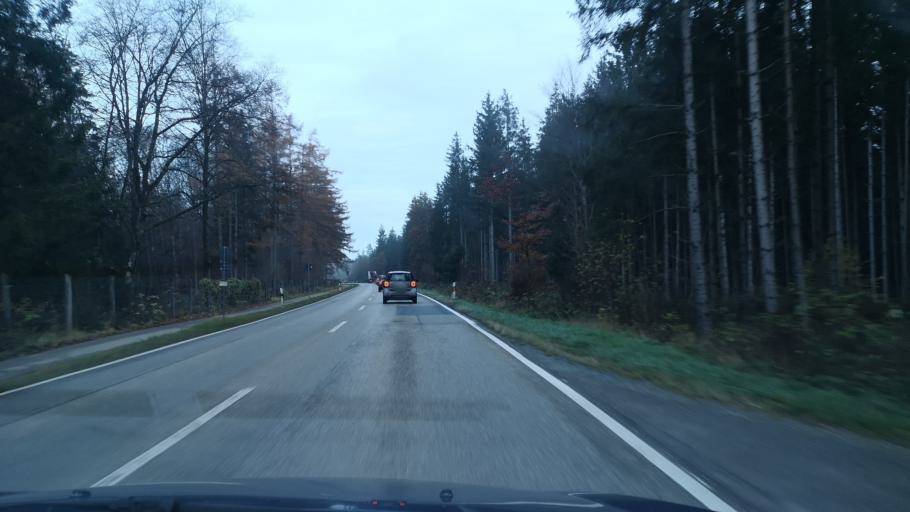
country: DE
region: Bavaria
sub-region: Upper Bavaria
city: Forstinning
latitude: 48.1461
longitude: 11.9215
